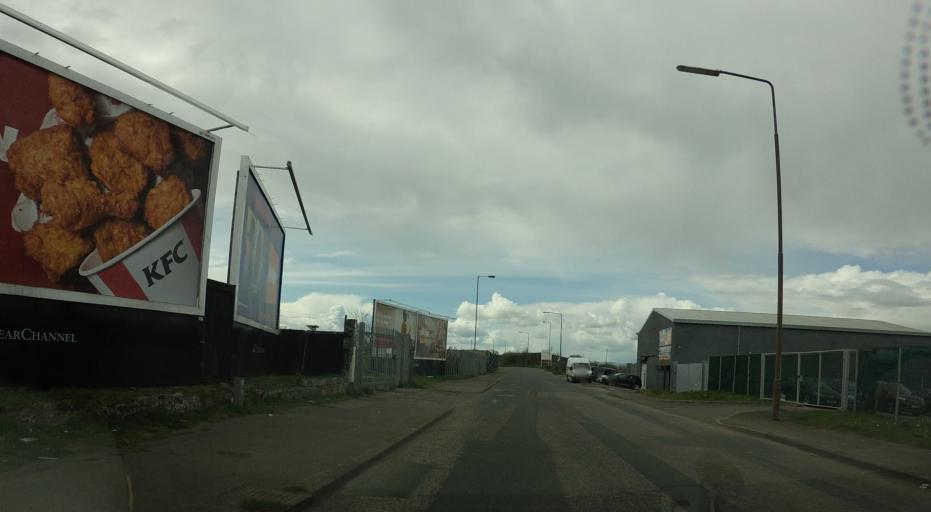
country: GB
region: Scotland
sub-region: Edinburgh
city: Edinburgh
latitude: 55.9828
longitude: -3.2323
